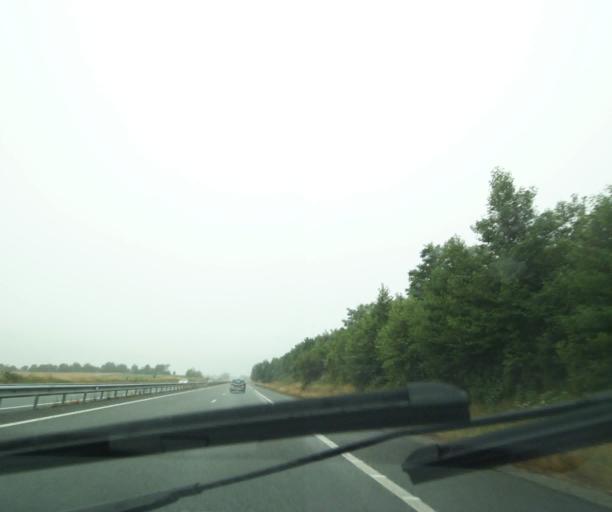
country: FR
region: Midi-Pyrenees
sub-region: Departement de l'Aveyron
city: Naucelle
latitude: 44.1330
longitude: 2.3092
